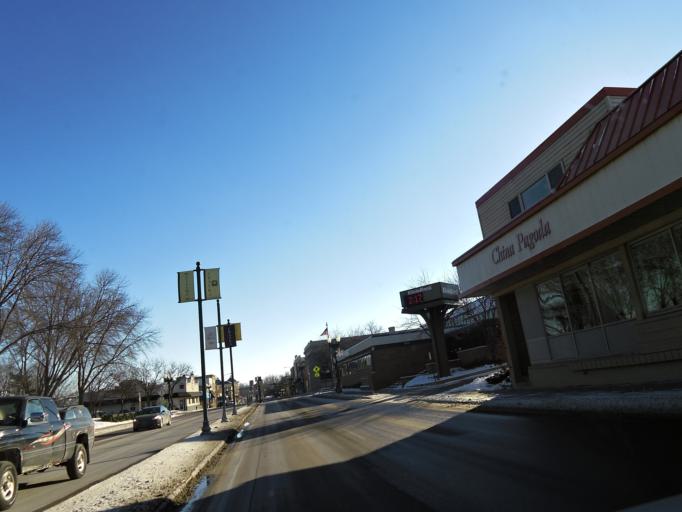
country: US
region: Minnesota
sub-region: Carver County
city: Chaska
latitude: 44.7871
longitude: -93.6011
